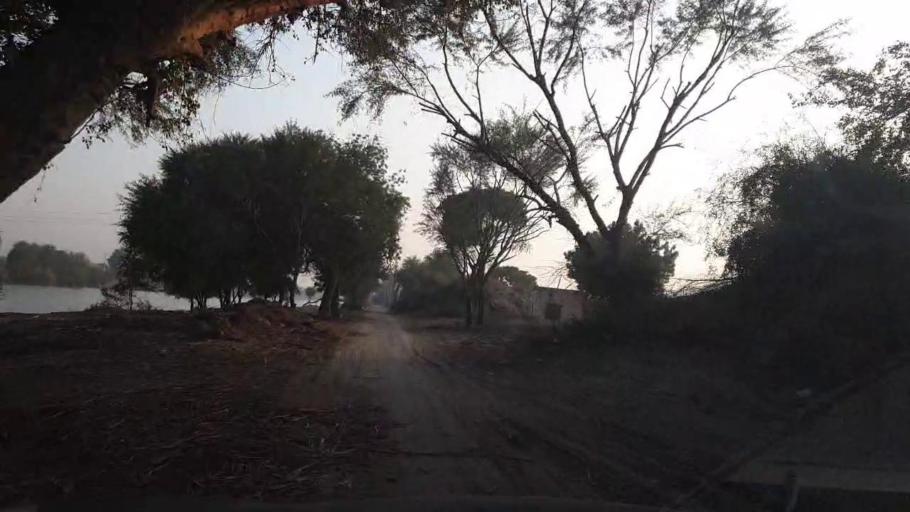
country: PK
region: Sindh
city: Ubauro
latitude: 28.3085
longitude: 69.7898
